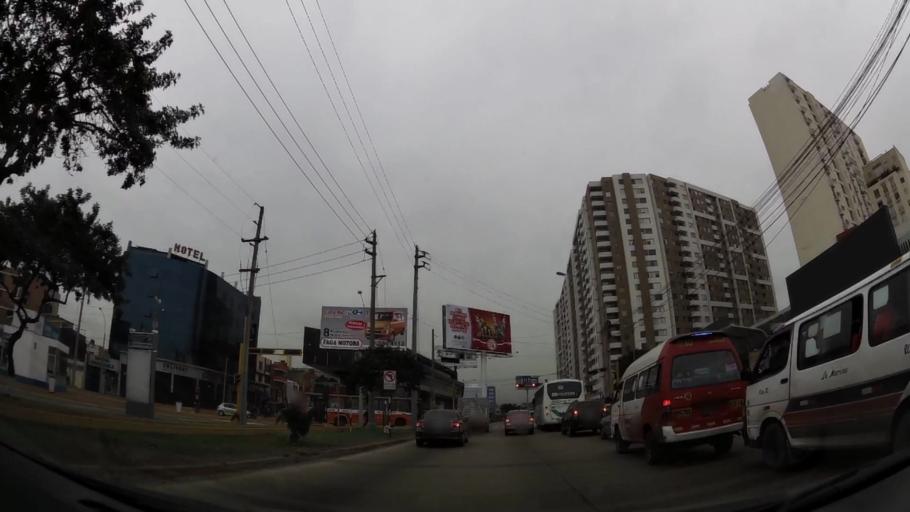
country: PE
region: Callao
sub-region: Callao
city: Callao
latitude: -12.0753
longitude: -77.0800
